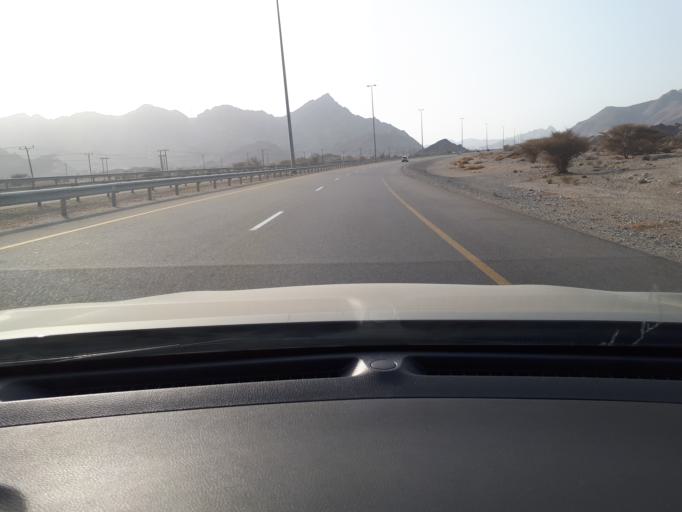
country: OM
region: Muhafazat Masqat
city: Muscat
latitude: 23.3337
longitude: 58.7050
